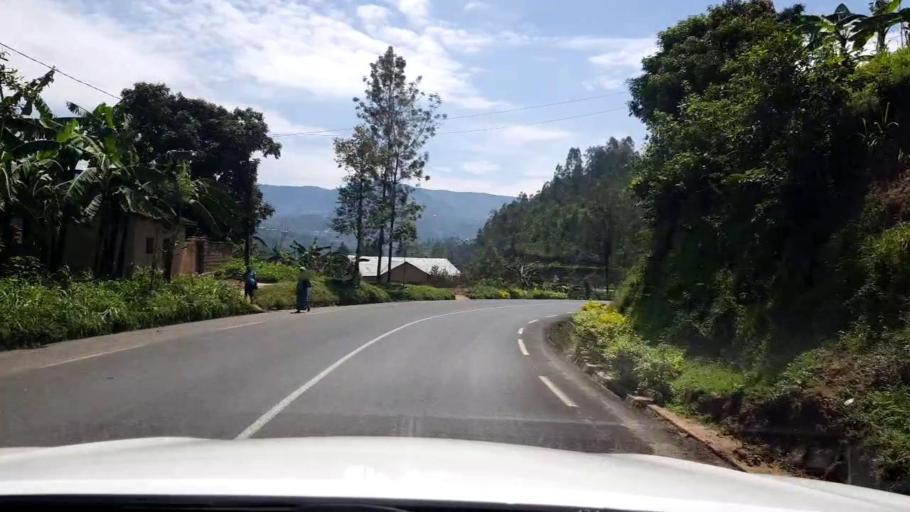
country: RW
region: Southern Province
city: Gitarama
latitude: -1.9208
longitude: 29.6486
